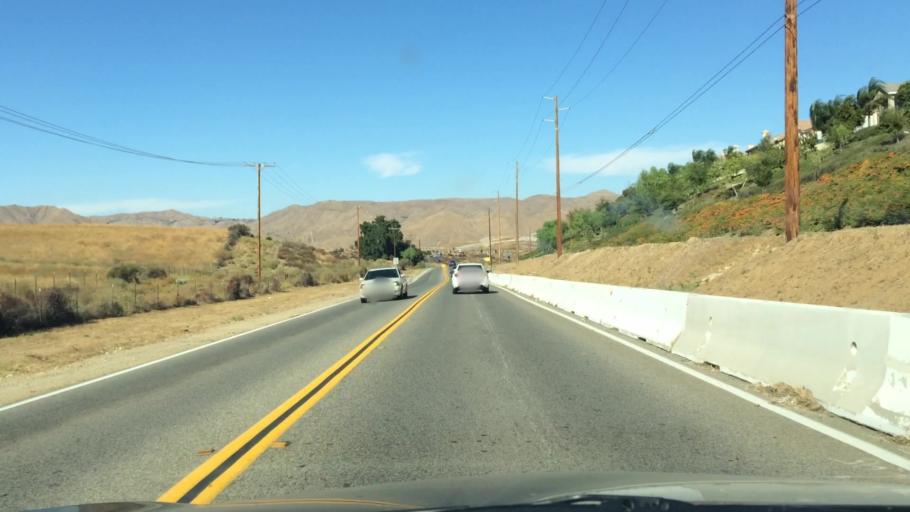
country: US
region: California
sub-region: Riverside County
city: Lake Elsinore
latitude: 33.7021
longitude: -117.3899
